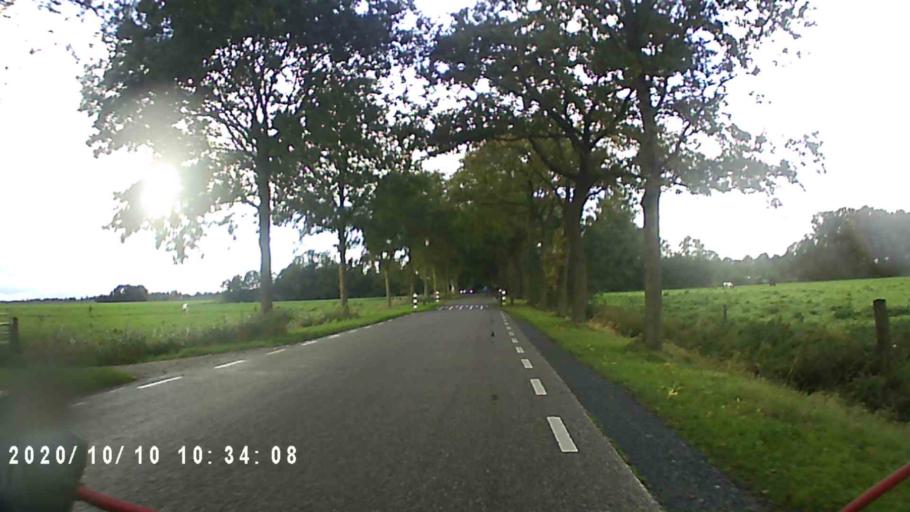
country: NL
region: Groningen
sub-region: Gemeente Grootegast
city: Grootegast
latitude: 53.1891
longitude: 6.3178
